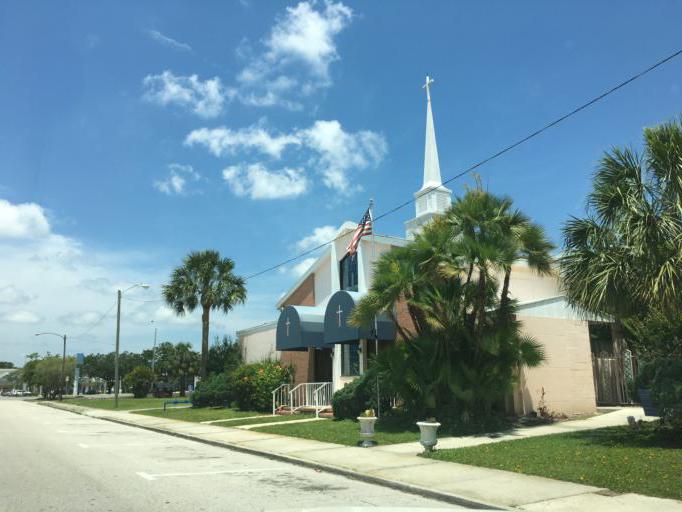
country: US
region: Florida
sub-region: Pinellas County
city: Lealman
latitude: 27.8058
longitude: -82.6372
